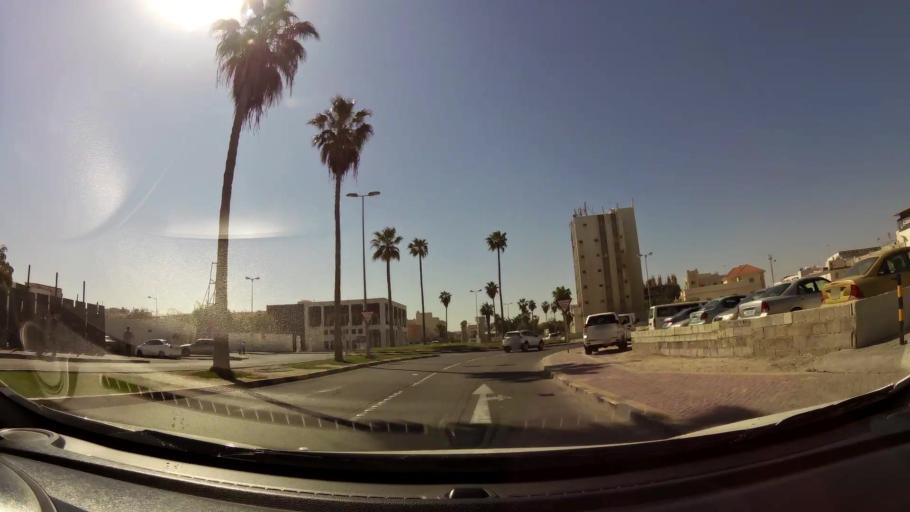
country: BH
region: Muharraq
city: Al Muharraq
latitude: 26.2539
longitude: 50.6082
